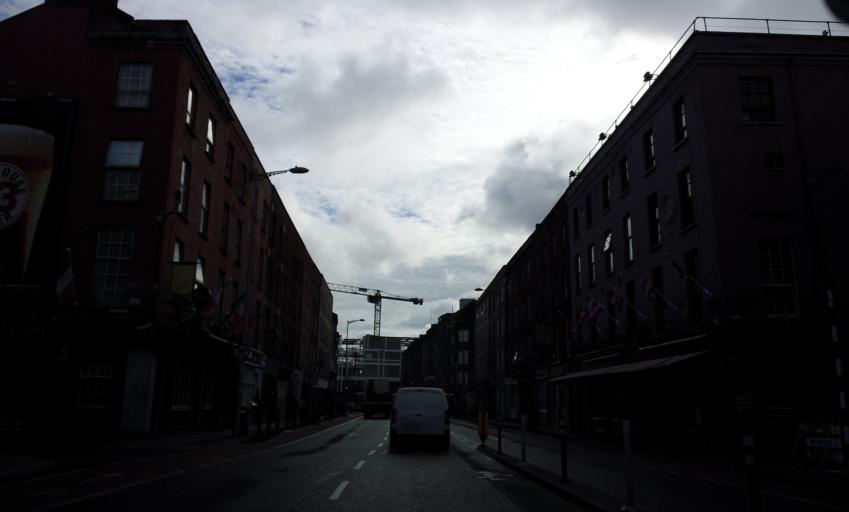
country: IE
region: Munster
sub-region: County Cork
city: Cork
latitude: 51.8975
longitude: -8.4787
